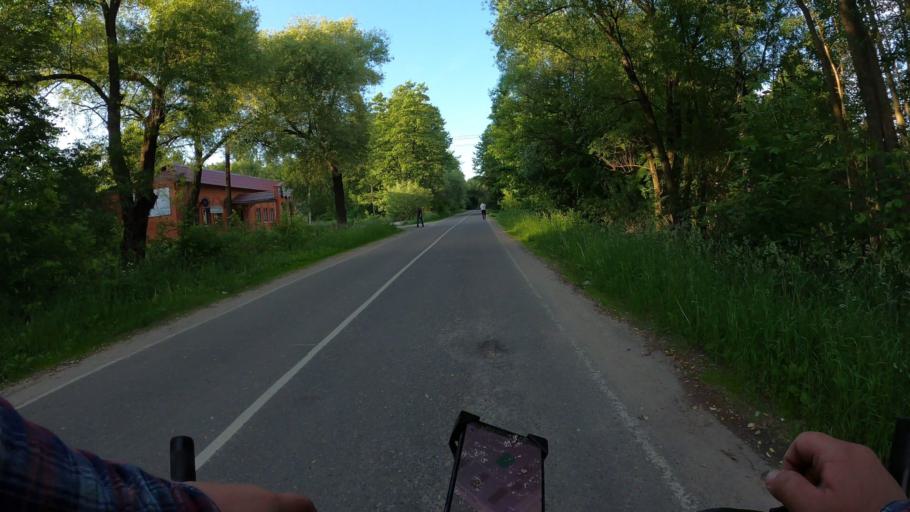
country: RU
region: Moskovskaya
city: Ashitkovo
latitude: 55.4305
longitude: 38.5619
